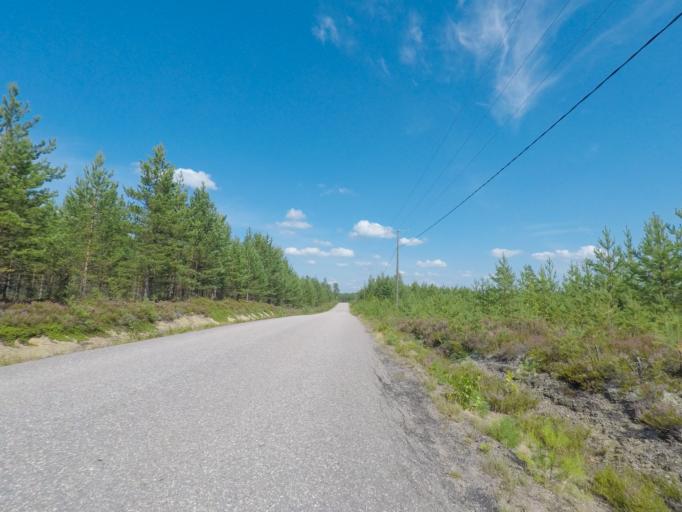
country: FI
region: Southern Savonia
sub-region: Mikkeli
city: Puumala
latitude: 61.4275
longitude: 28.1622
